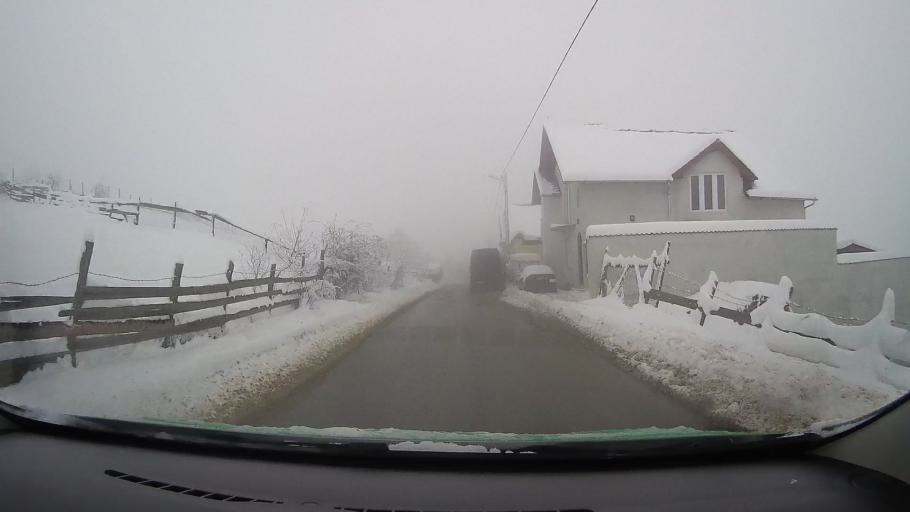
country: RO
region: Sibiu
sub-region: Comuna Jina
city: Jina
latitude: 45.7767
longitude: 23.6684
